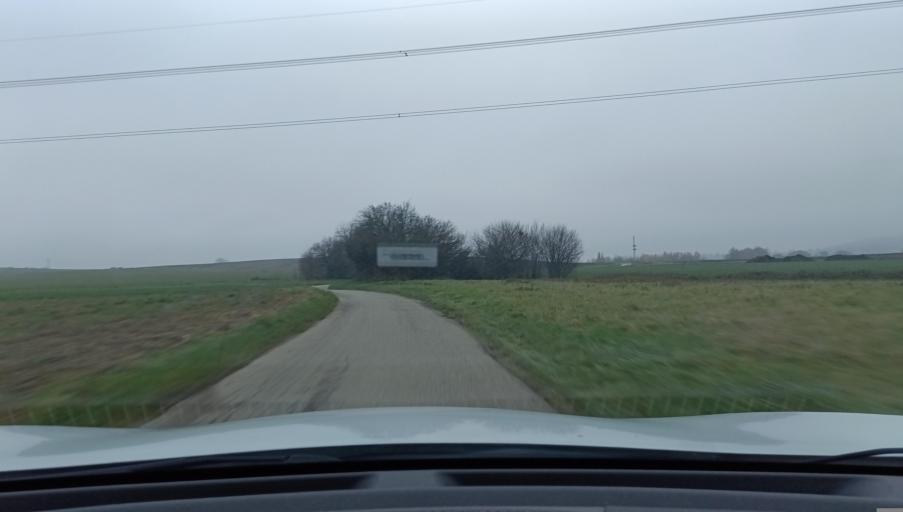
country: FR
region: Rhone-Alpes
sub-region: Departement de l'Isere
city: Seyssuel
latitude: 45.5805
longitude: 4.8479
